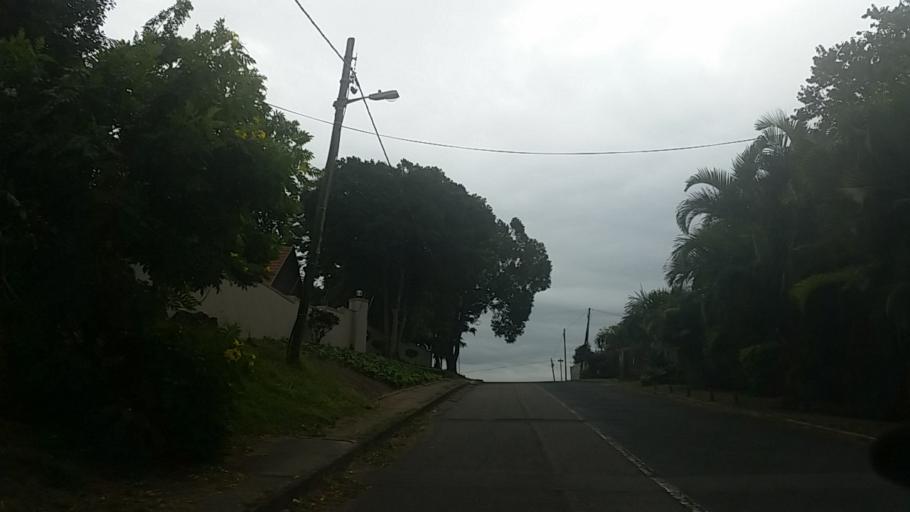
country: ZA
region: KwaZulu-Natal
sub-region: eThekwini Metropolitan Municipality
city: Berea
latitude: -29.8443
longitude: 30.9303
